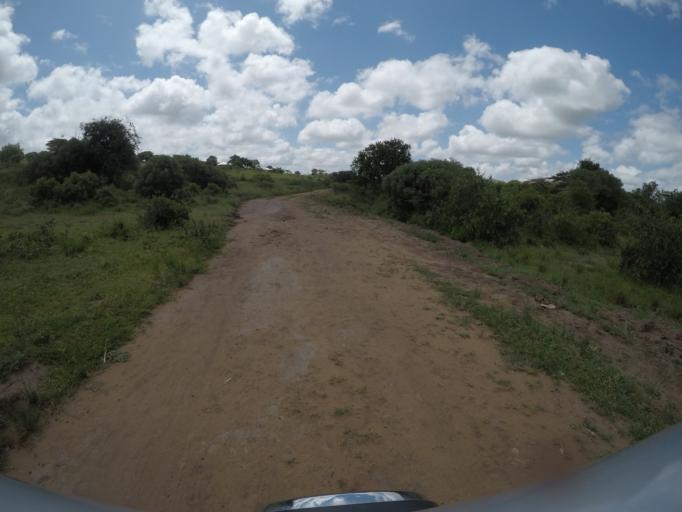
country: ZA
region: KwaZulu-Natal
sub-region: uThungulu District Municipality
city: Empangeni
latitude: -28.5889
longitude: 31.8395
